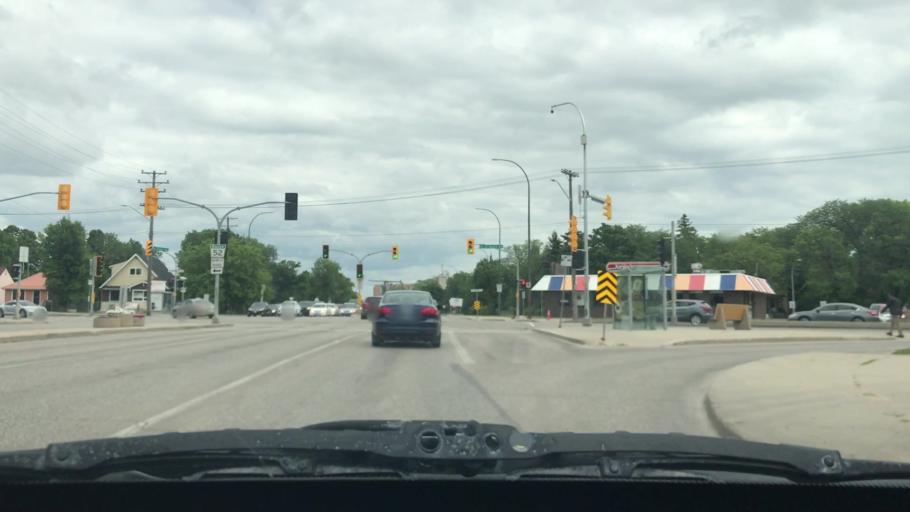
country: CA
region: Manitoba
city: Winnipeg
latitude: 49.8523
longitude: -97.1126
